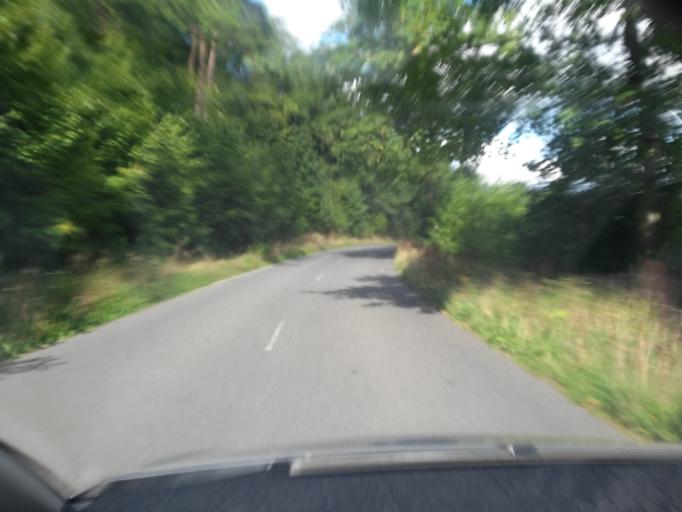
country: BE
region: Wallonia
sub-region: Province du Luxembourg
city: Libin
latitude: 50.0282
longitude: 5.3056
